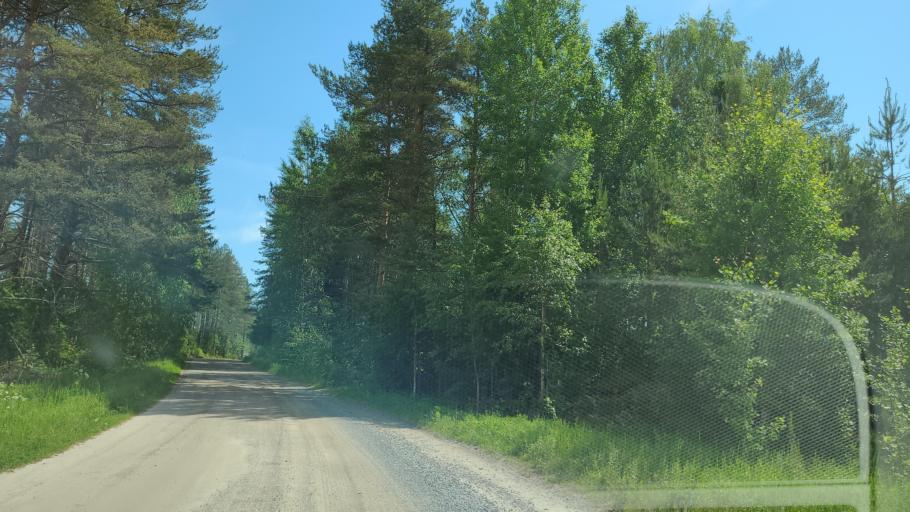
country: SE
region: Vaesterbotten
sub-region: Robertsfors Kommun
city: Robertsfors
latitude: 64.2262
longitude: 21.0208
